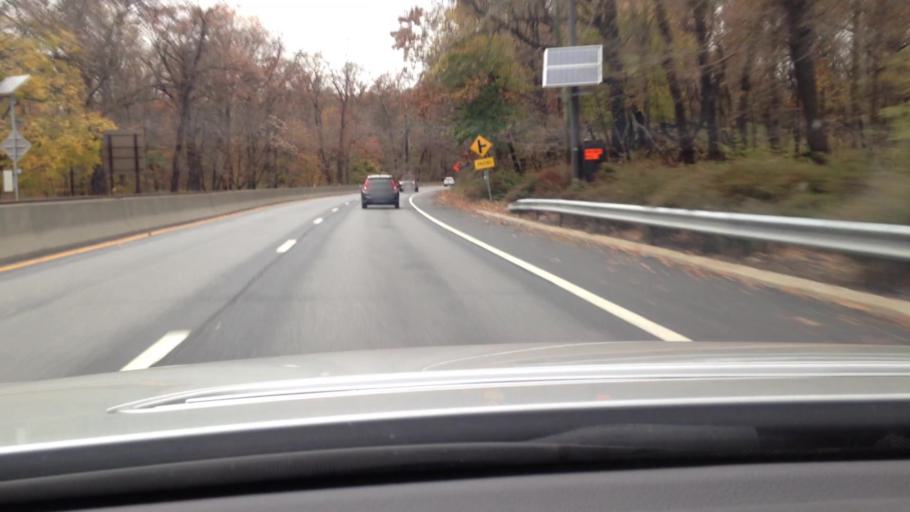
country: US
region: New York
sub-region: Westchester County
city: Elmsford
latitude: 41.0643
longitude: -73.8238
